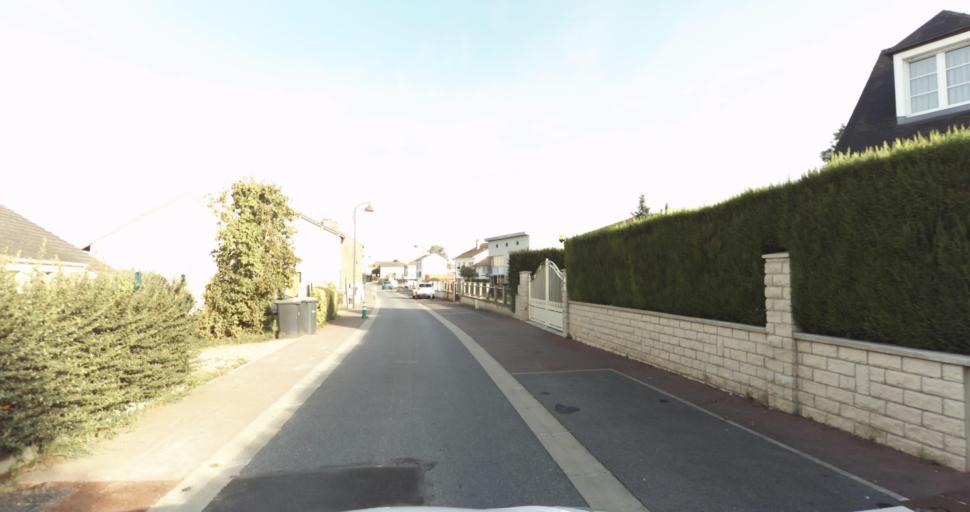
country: FR
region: Champagne-Ardenne
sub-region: Departement des Ardennes
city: Villers-Semeuse
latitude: 49.7407
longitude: 4.7468
